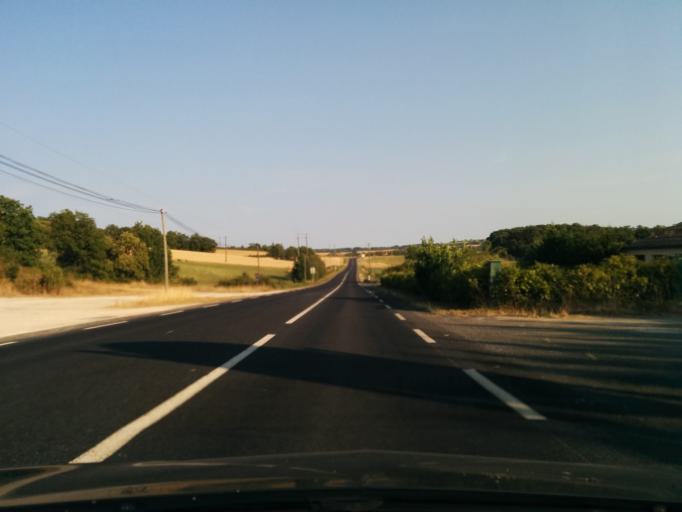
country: FR
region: Midi-Pyrenees
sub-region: Departement du Lot
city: Le Vigan
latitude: 44.7544
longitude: 1.4958
